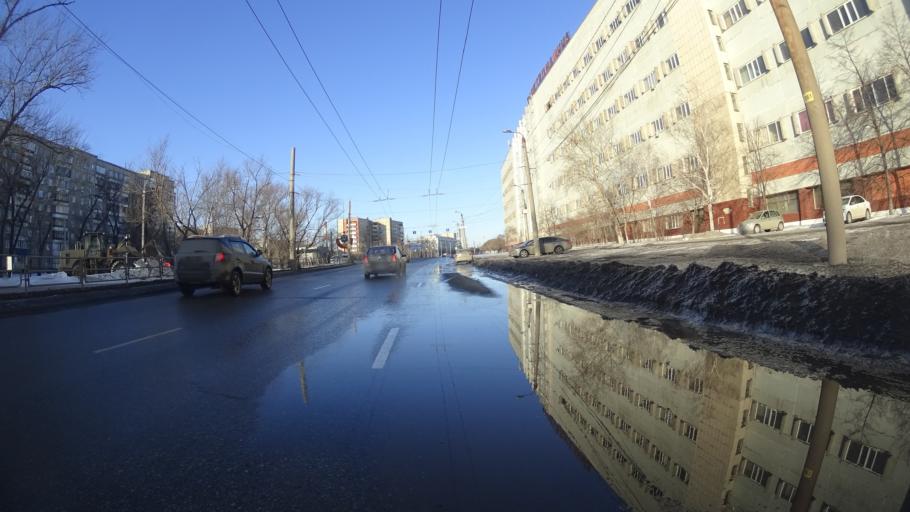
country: RU
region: Chelyabinsk
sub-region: Gorod Chelyabinsk
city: Chelyabinsk
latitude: 55.1241
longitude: 61.4752
